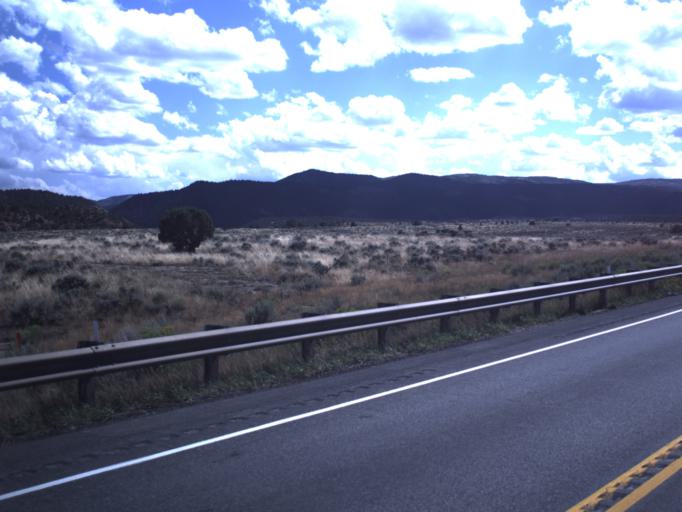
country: US
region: Utah
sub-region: Duchesne County
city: Duchesne
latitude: 40.2072
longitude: -110.7690
